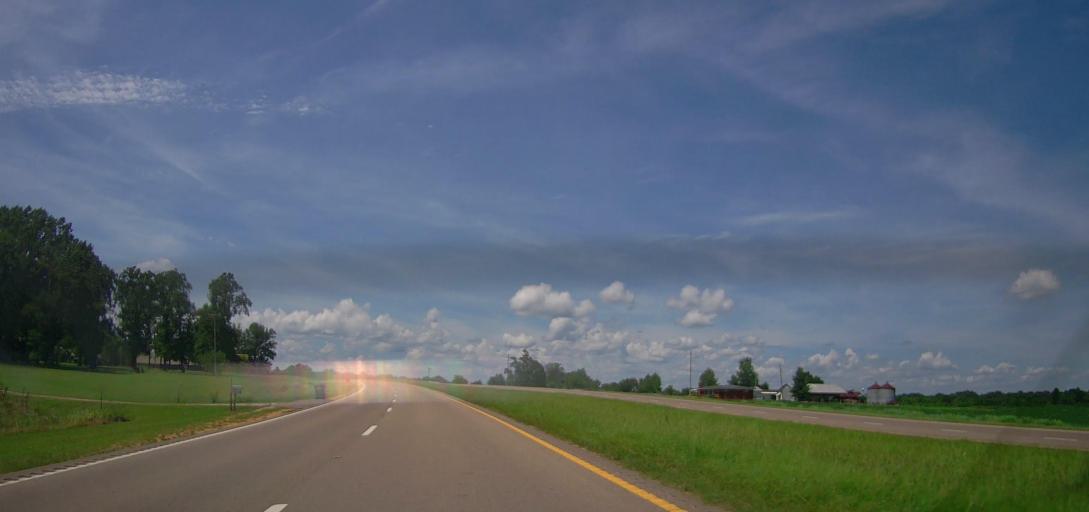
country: US
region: Mississippi
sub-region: Lee County
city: Nettleton
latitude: 33.9751
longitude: -88.6139
